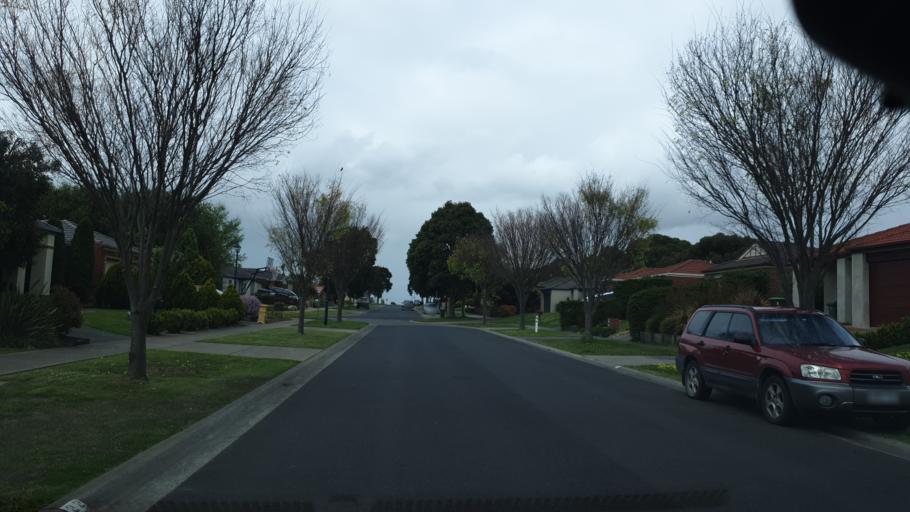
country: AU
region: Victoria
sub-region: Casey
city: Cranbourne East
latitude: -38.1075
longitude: 145.2947
